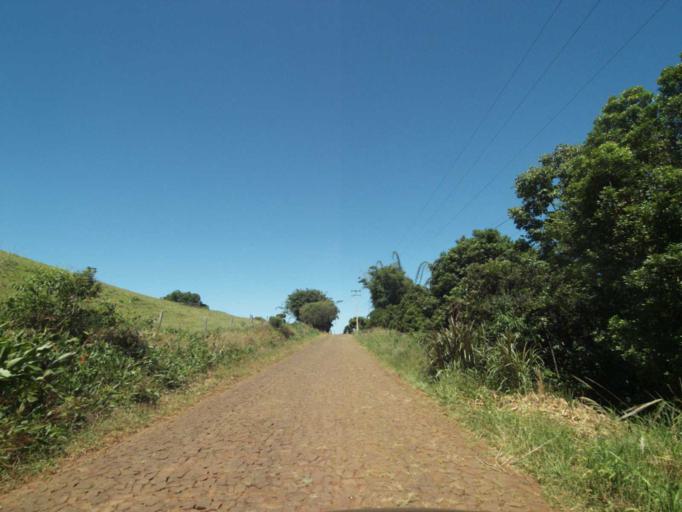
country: BR
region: Parana
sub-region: Coronel Vivida
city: Coronel Vivida
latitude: -25.9656
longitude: -52.8211
